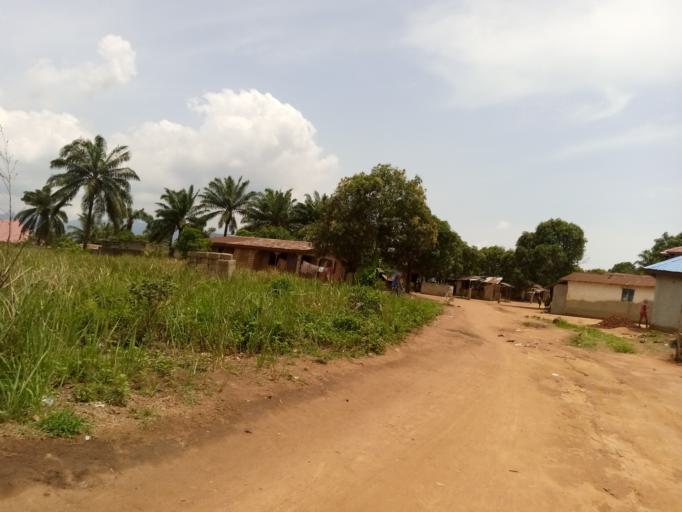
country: SL
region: Western Area
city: Waterloo
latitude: 8.3295
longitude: -13.0423
